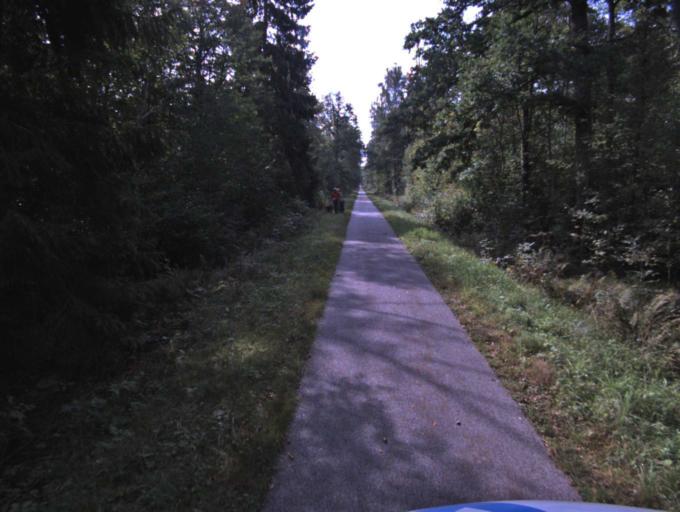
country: SE
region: Vaestra Goetaland
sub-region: Tranemo Kommun
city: Limmared
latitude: 57.6553
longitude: 13.3620
